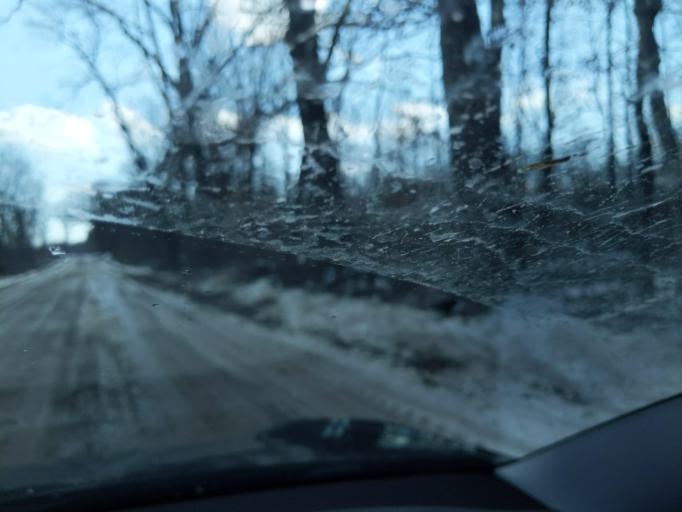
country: US
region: Michigan
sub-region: Livingston County
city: Fowlerville
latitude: 42.5594
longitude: -84.0885
